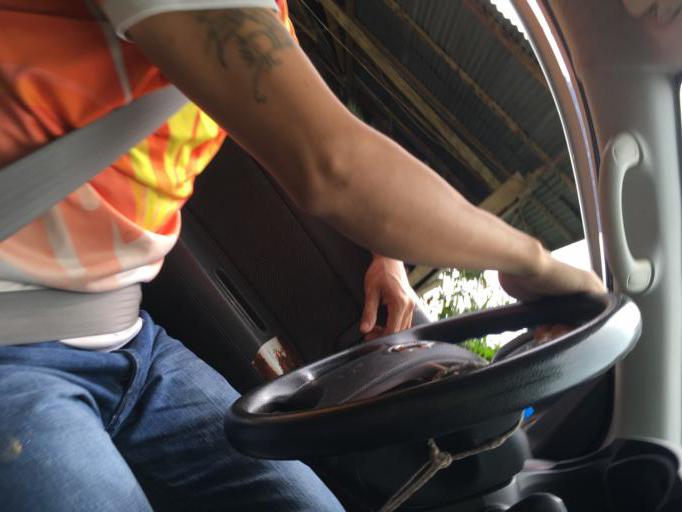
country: LA
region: Phongsali
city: Phongsali
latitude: 21.4476
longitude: 102.1614
